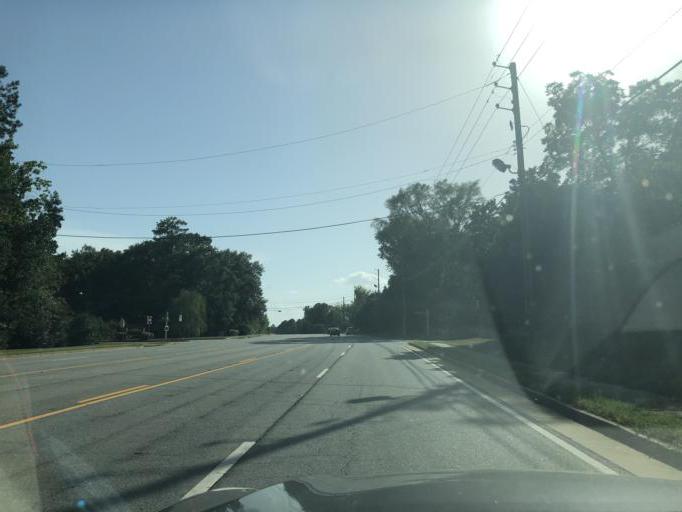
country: US
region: Georgia
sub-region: Muscogee County
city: Columbus
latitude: 32.5013
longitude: -84.9020
